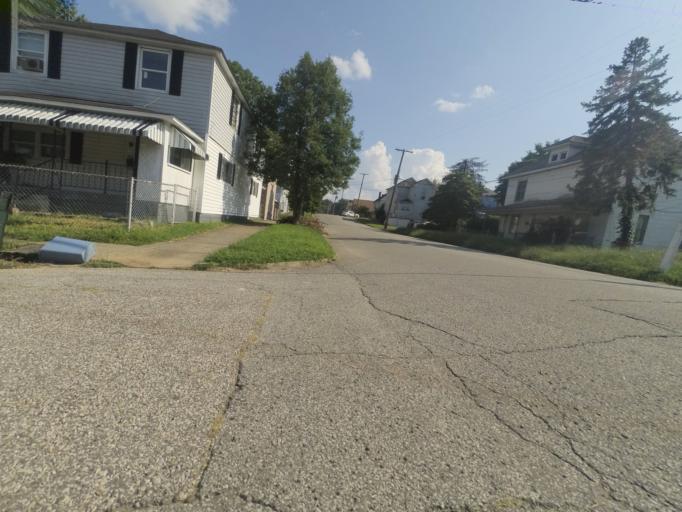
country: US
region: West Virginia
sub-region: Cabell County
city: Huntington
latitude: 38.4118
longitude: -82.4763
